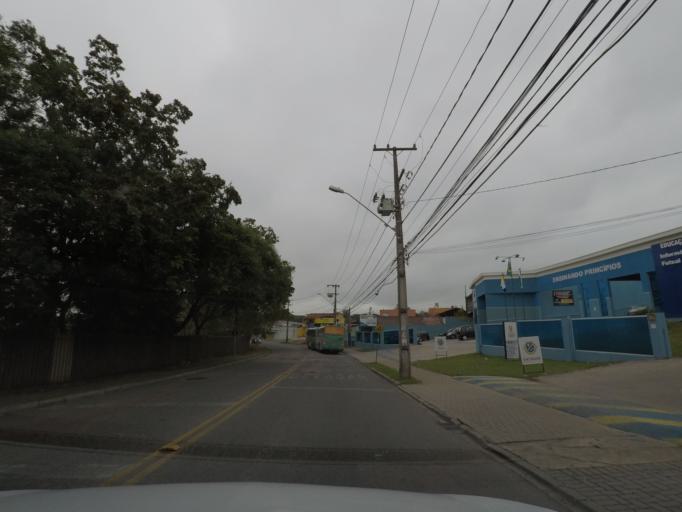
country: BR
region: Parana
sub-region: Curitiba
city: Curitiba
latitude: -25.4566
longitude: -49.3475
